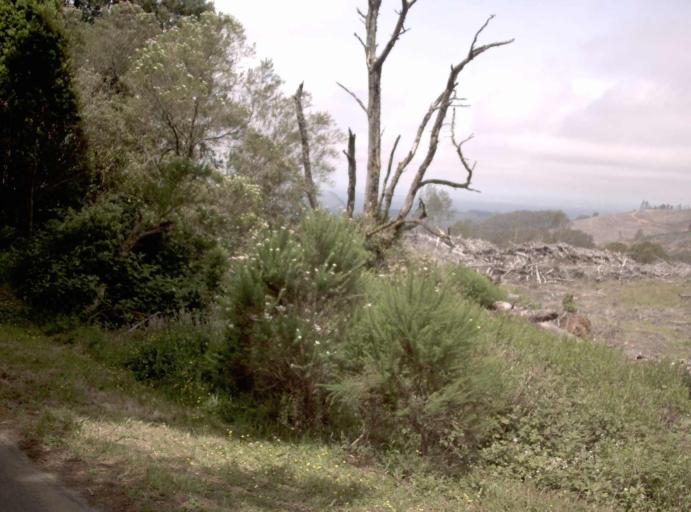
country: AU
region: Victoria
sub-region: Latrobe
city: Traralgon
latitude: -38.4236
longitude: 146.6032
